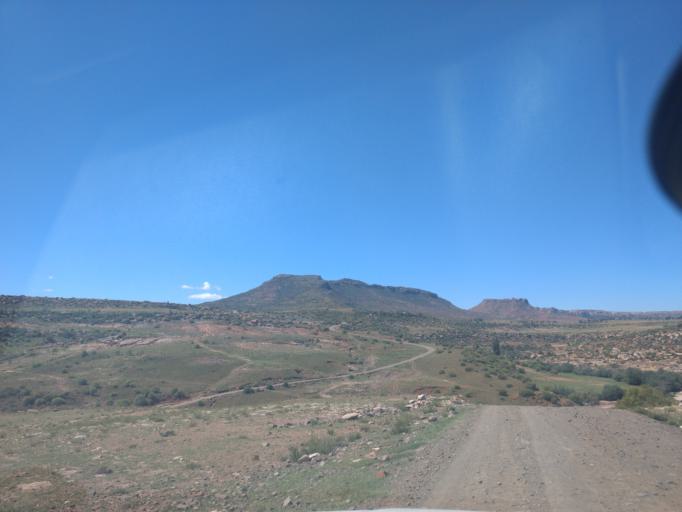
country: LS
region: Maseru
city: Maseru
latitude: -29.4848
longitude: 27.3701
